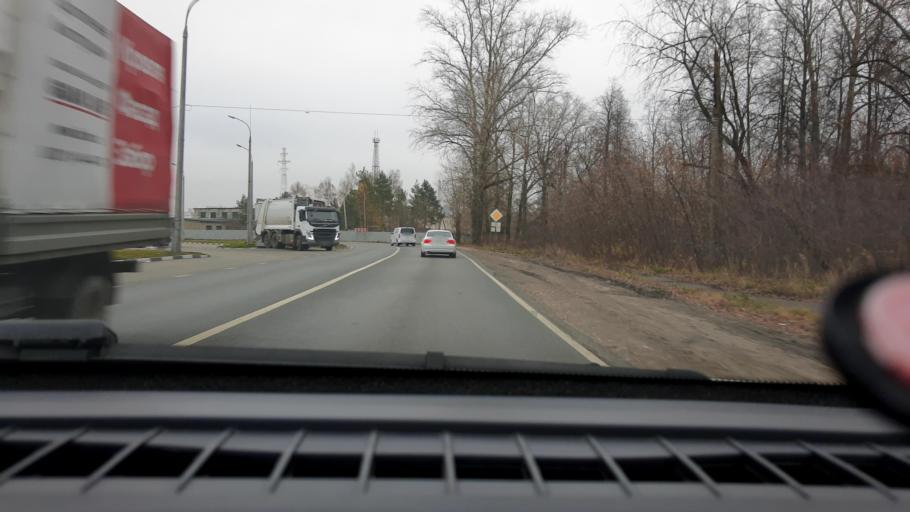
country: RU
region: Nizjnij Novgorod
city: Novaya Balakhna
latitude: 56.5045
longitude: 43.5913
